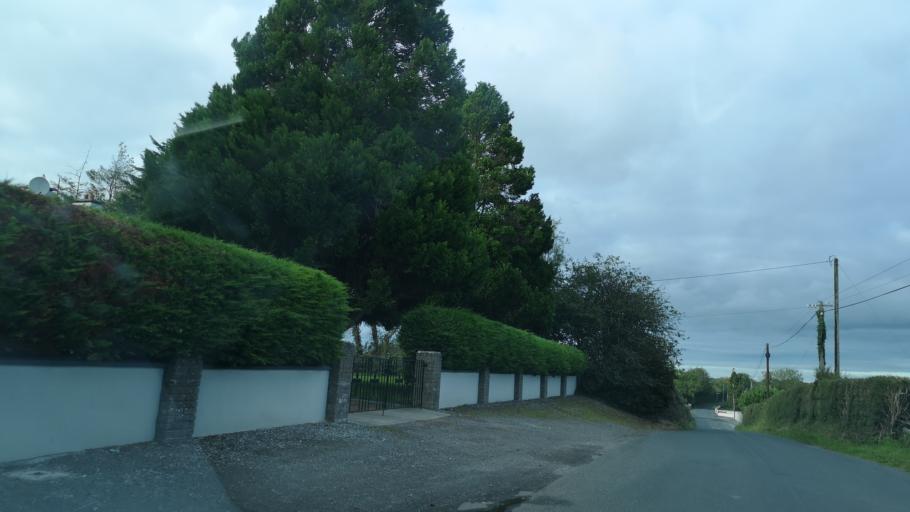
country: IE
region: Connaught
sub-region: County Galway
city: Ballinasloe
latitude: 53.3262
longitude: -8.1007
